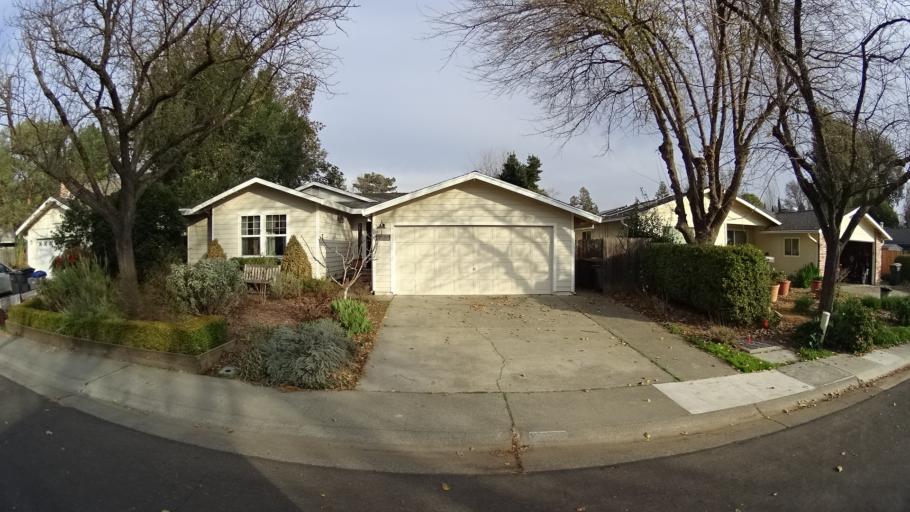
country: US
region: California
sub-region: Yolo County
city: Davis
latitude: 38.5613
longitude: -121.7147
